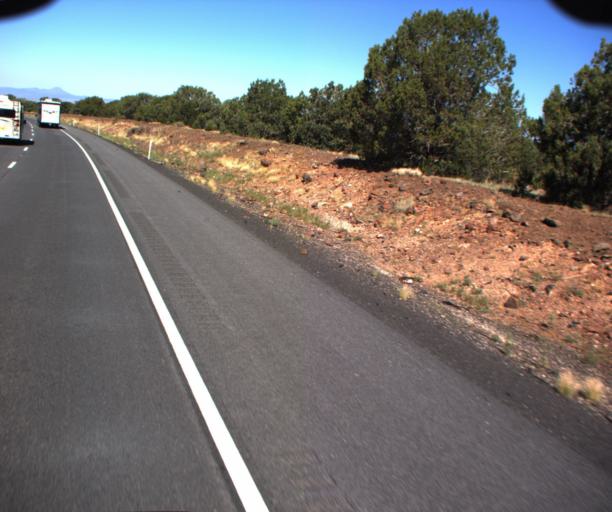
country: US
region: Arizona
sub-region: Coconino County
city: Williams
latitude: 35.2172
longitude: -112.3707
